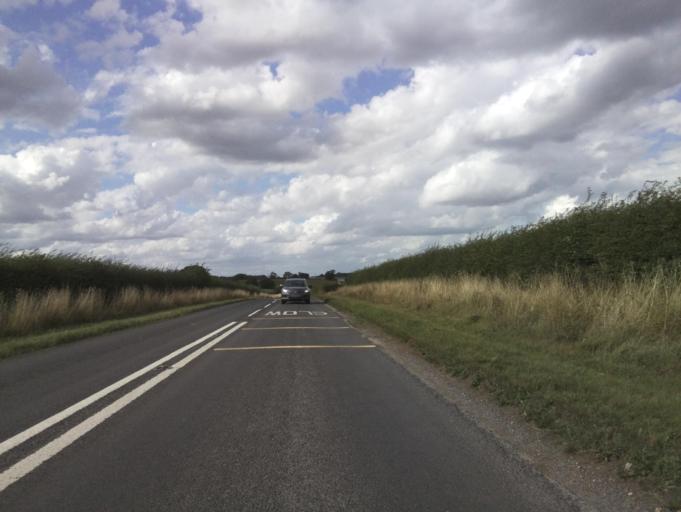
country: GB
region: England
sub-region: North Yorkshire
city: Ripon
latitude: 54.1630
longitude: -1.5458
